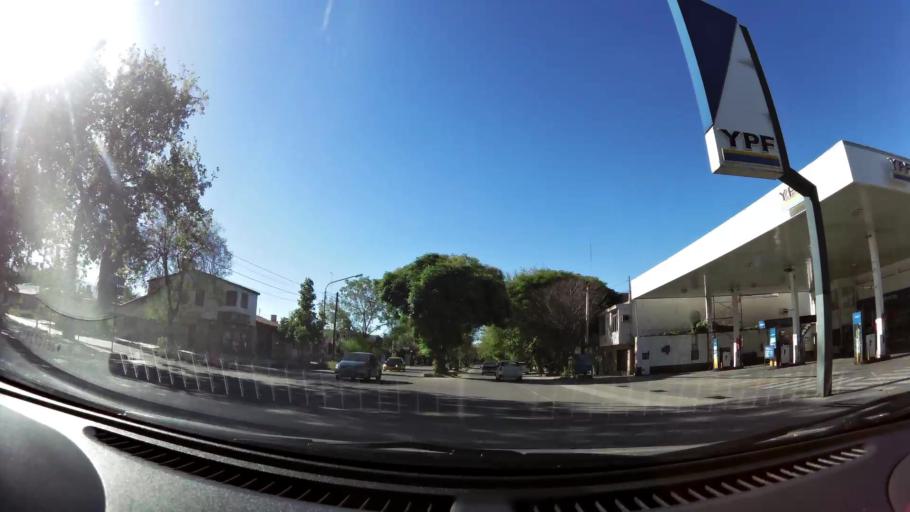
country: AR
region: Mendoza
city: Las Heras
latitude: -32.8571
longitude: -68.8214
